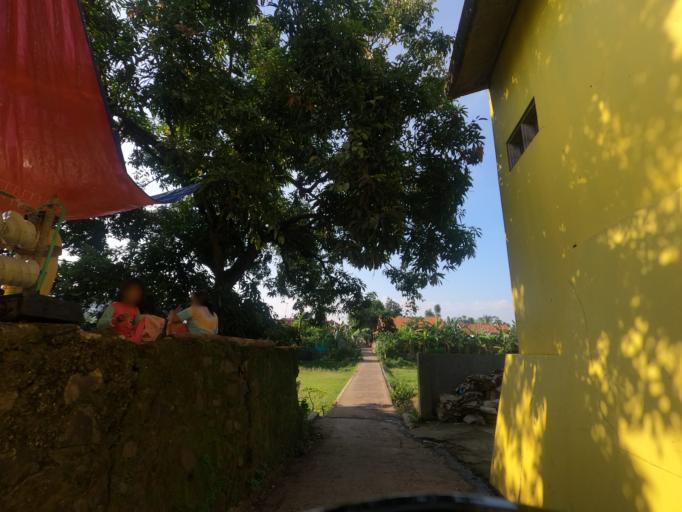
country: ID
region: West Java
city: Pamanukan
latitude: -6.5548
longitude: 107.8260
